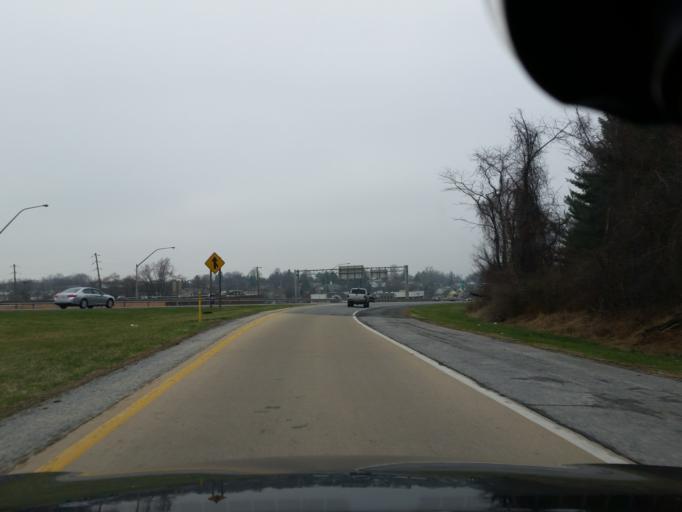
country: US
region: Pennsylvania
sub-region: Cumberland County
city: Mechanicsburg
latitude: 40.1797
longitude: -76.9858
